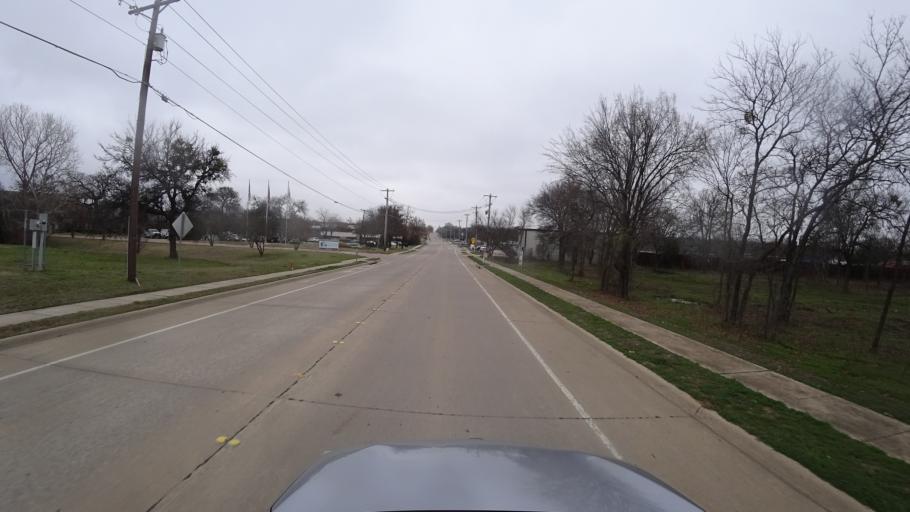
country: US
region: Texas
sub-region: Denton County
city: Lewisville
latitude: 33.0559
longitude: -96.9927
